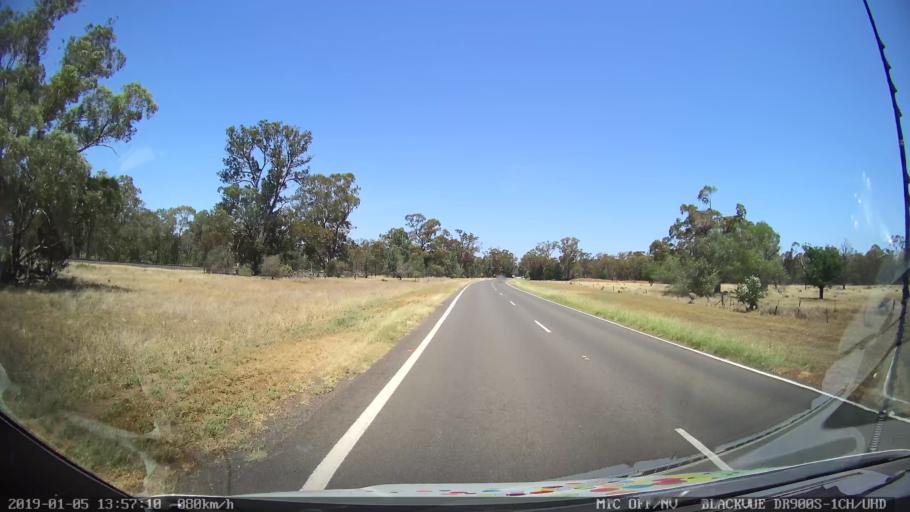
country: AU
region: New South Wales
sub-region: Gunnedah
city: Gunnedah
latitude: -31.1246
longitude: 150.2729
